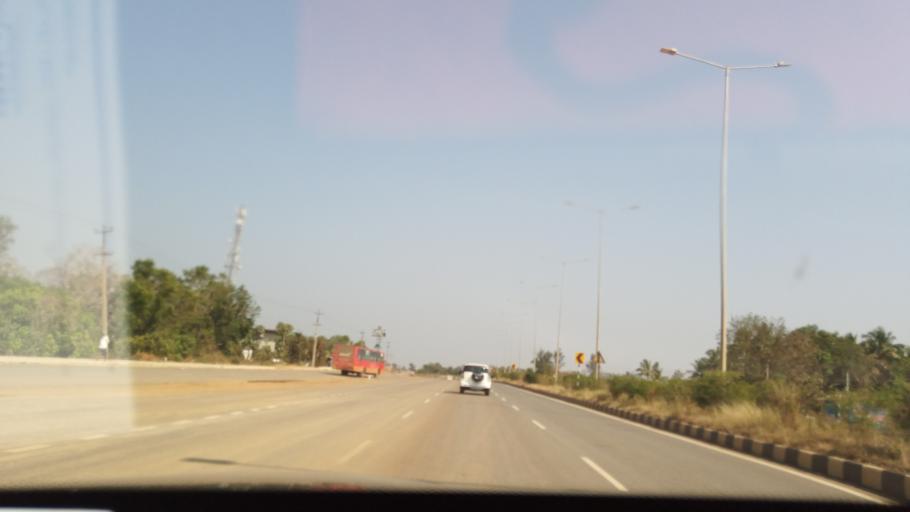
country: IN
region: Karnataka
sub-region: Dharwad
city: Kundgol
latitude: 15.1660
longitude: 75.1411
